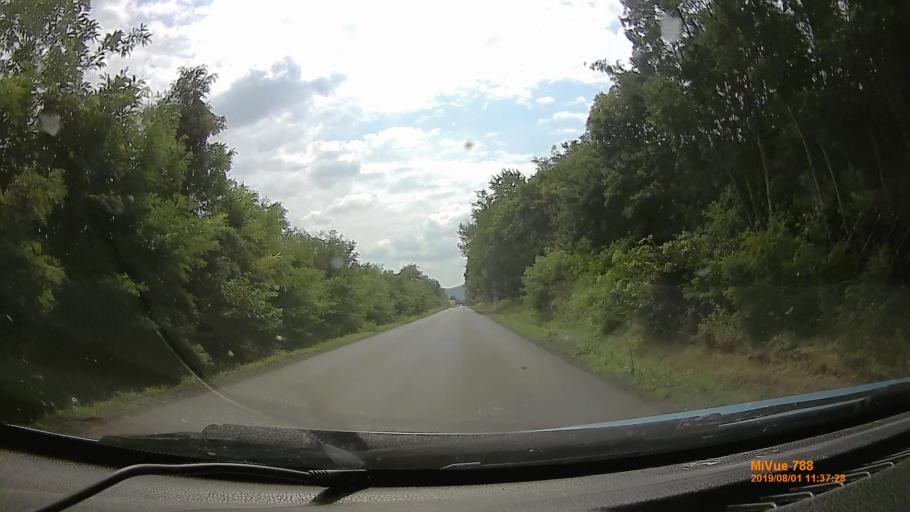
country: HU
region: Baranya
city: Villany
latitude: 45.9064
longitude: 18.3832
